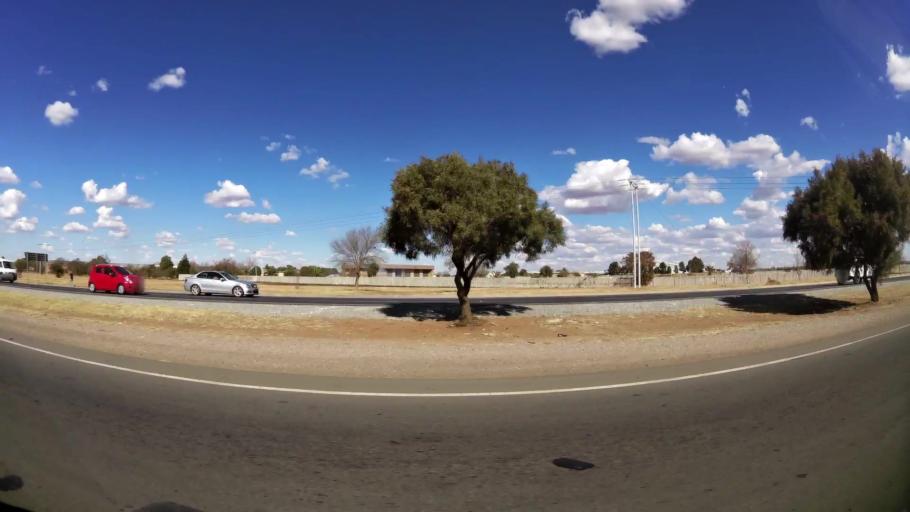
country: ZA
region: North-West
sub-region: Dr Kenneth Kaunda District Municipality
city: Klerksdorp
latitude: -26.8695
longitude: 26.6217
